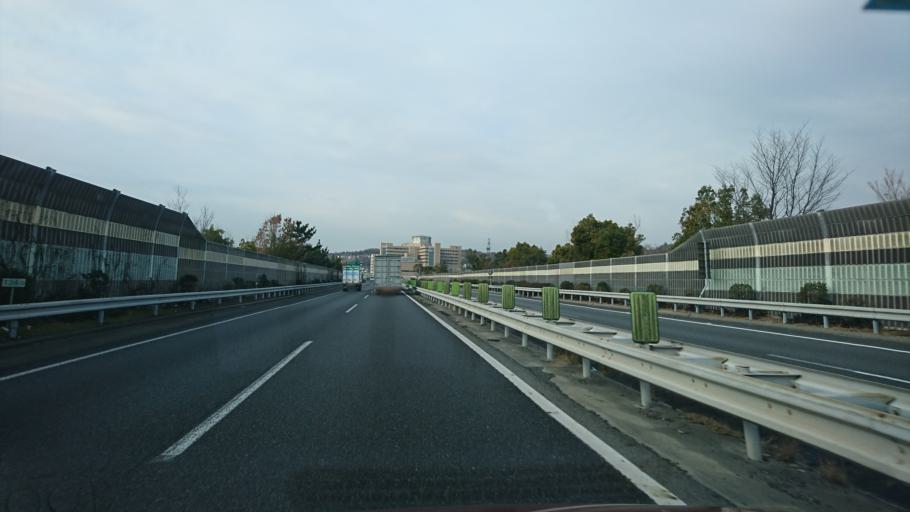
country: JP
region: Okayama
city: Okayama-shi
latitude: 34.7087
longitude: 133.9071
